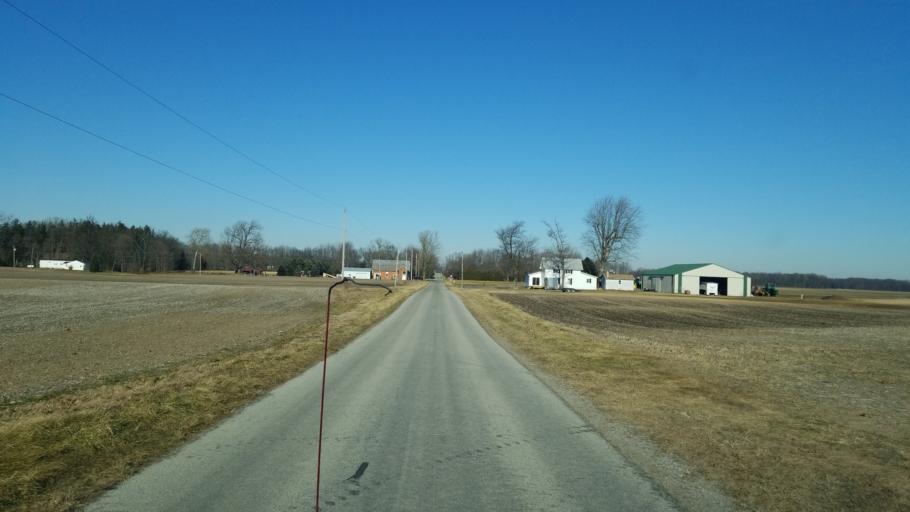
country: US
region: Ohio
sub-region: Henry County
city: Liberty Center
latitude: 41.3905
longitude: -83.9706
